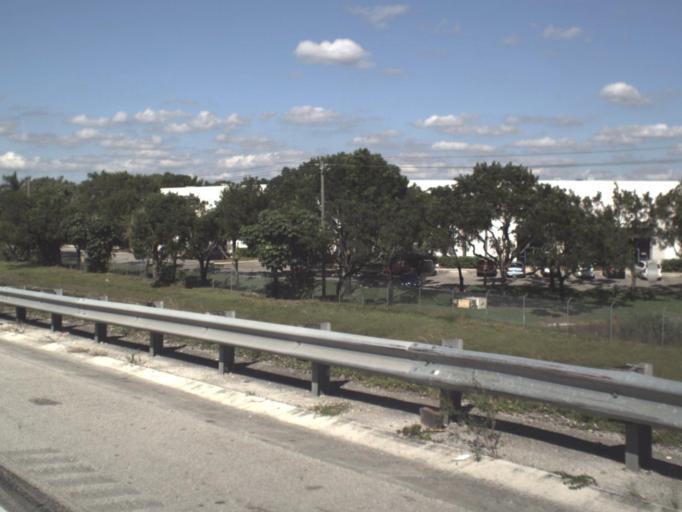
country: US
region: Florida
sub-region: Miami-Dade County
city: Lake Lucerne
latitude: 25.9715
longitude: -80.2803
